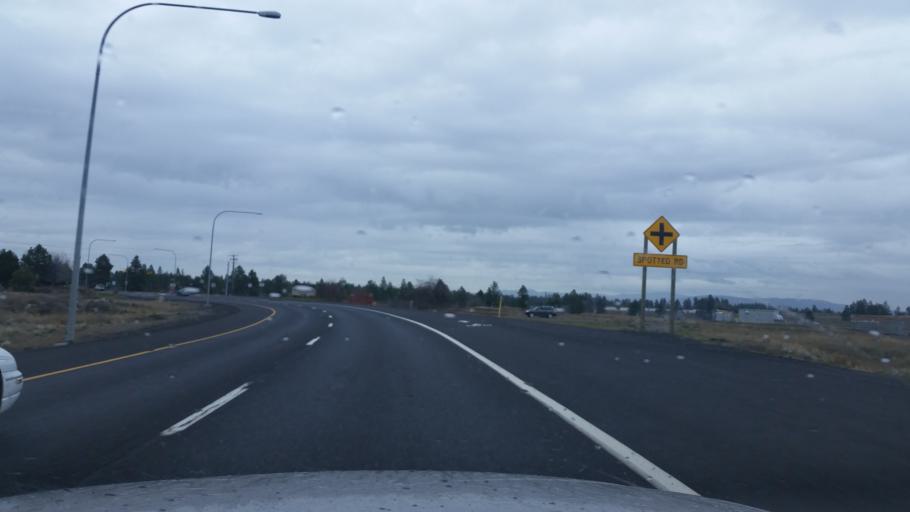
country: US
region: Washington
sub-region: Spokane County
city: Airway Heights
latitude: 47.6346
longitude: -117.5199
